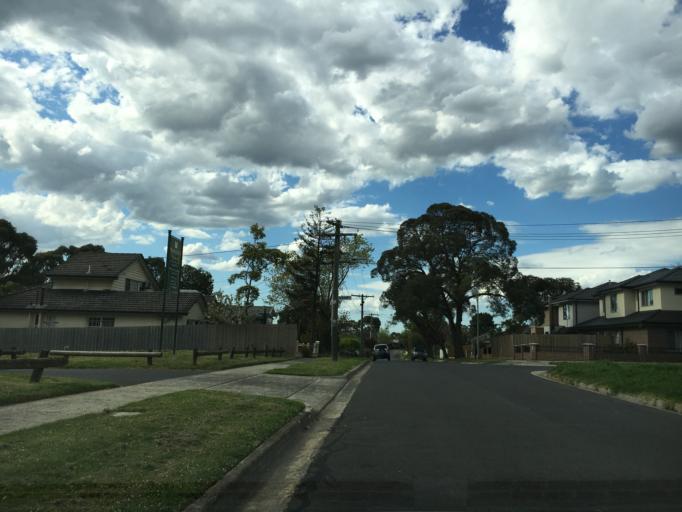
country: AU
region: Victoria
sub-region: Monash
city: Chadstone
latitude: -37.8881
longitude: 145.1179
